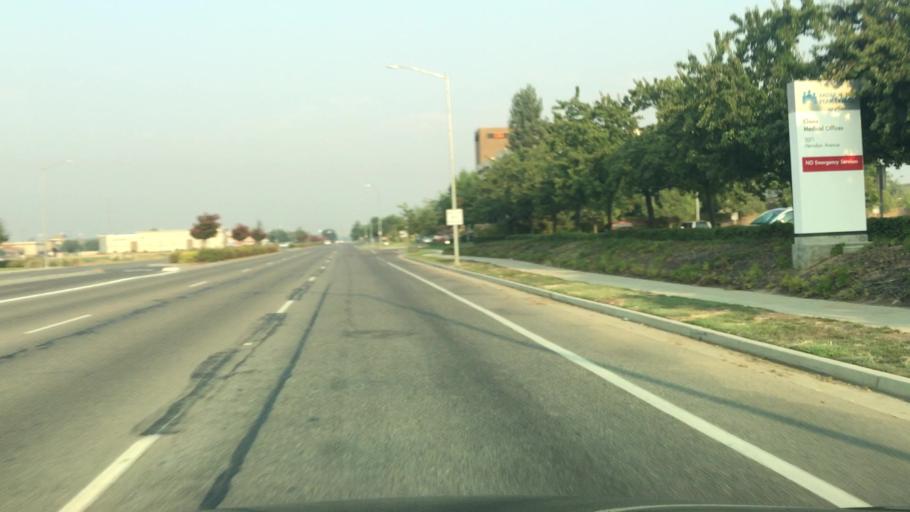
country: US
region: California
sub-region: Fresno County
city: Clovis
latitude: 36.8376
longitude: -119.6783
